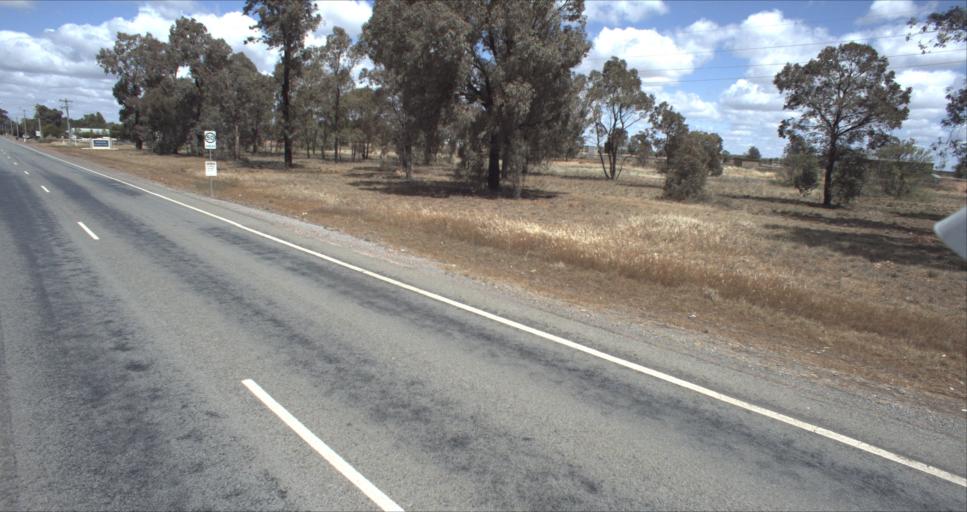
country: AU
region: New South Wales
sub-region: Murrumbidgee Shire
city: Darlington Point
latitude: -34.5086
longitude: 146.1867
